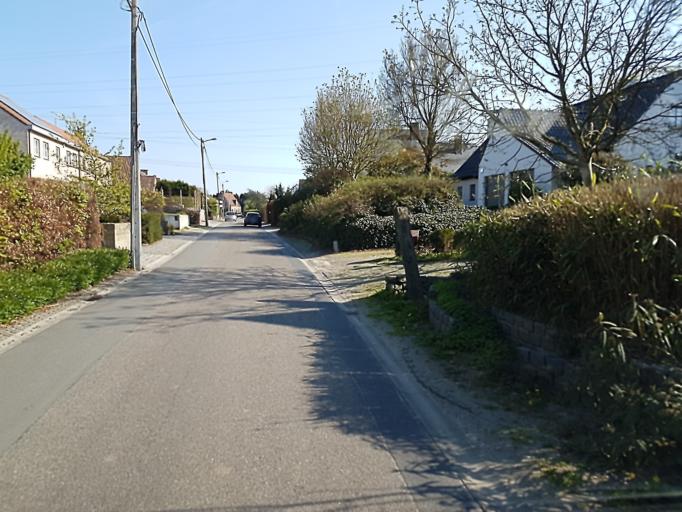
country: BE
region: Flanders
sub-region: Provincie Oost-Vlaanderen
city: Temse
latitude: 51.1411
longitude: 4.2192
